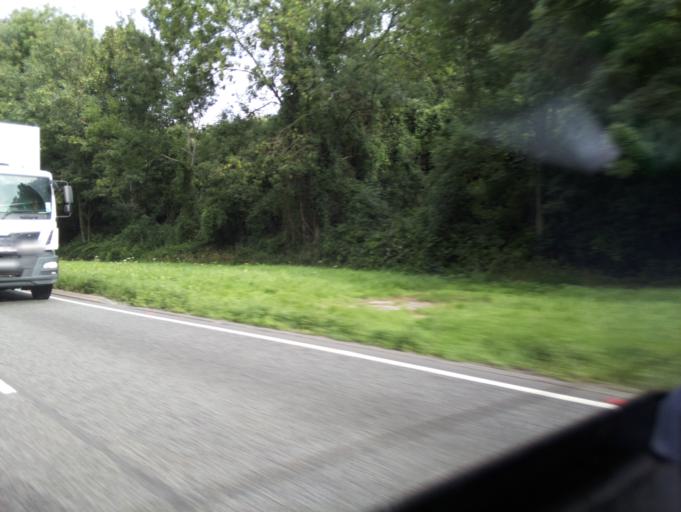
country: GB
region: England
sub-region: Gloucestershire
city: Shurdington
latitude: 51.8400
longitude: -2.1076
